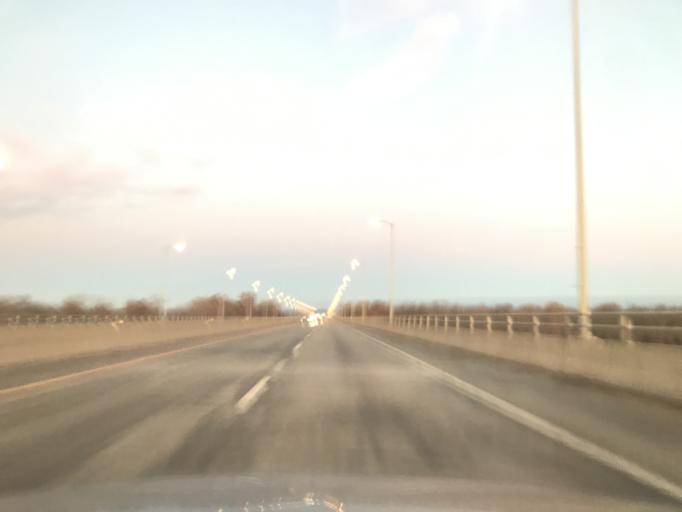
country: US
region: Missouri
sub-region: Marion County
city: Hannibal
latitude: 39.7204
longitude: -91.3577
